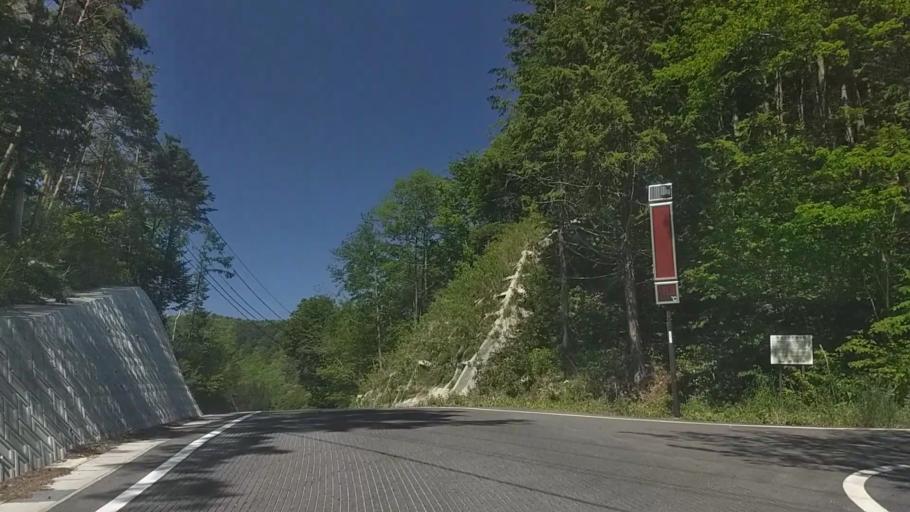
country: JP
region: Yamanashi
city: Nirasaki
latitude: 35.8696
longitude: 138.4519
